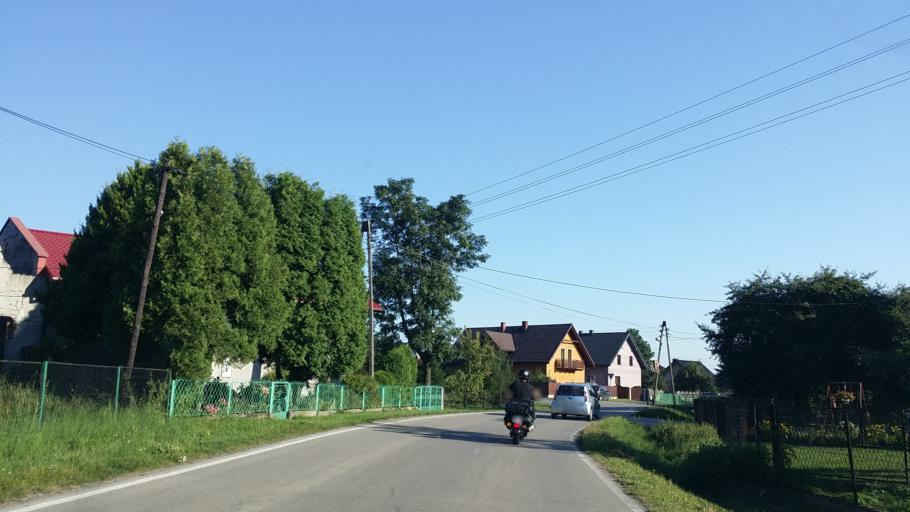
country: PL
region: Lesser Poland Voivodeship
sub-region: Powiat chrzanowski
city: Babice
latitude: 50.0295
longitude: 19.4633
